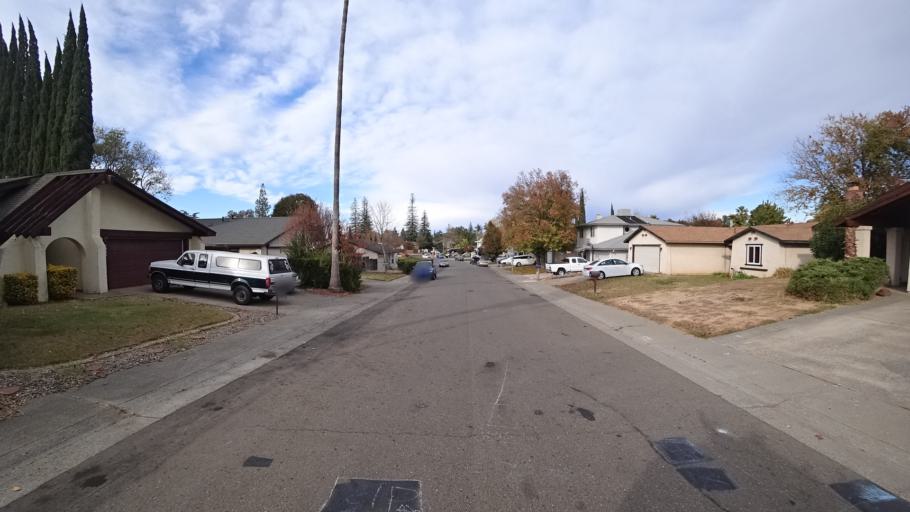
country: US
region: California
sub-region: Sacramento County
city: Citrus Heights
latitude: 38.7087
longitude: -121.2577
